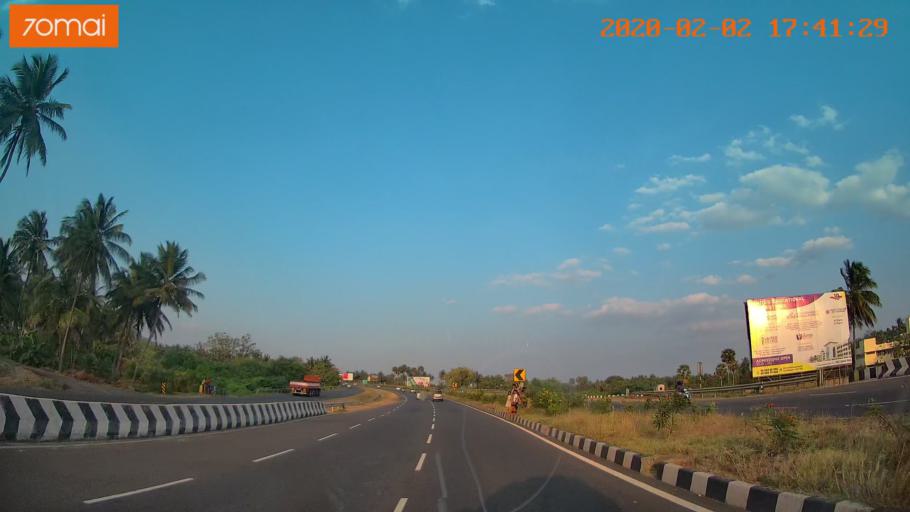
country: IN
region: Tamil Nadu
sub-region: Coimbatore
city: Madukkarai
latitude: 10.8748
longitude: 76.9017
